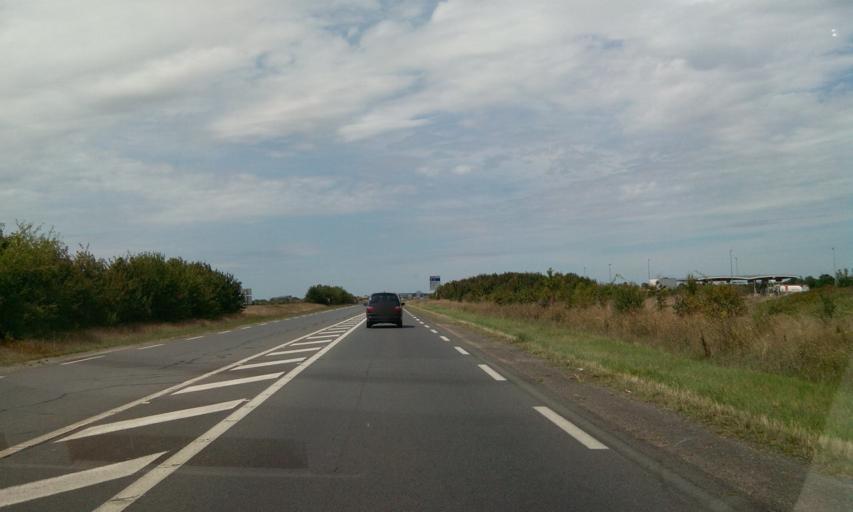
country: FR
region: Poitou-Charentes
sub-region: Departement des Deux-Sevres
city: Vouille
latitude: 46.3057
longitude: -0.3639
